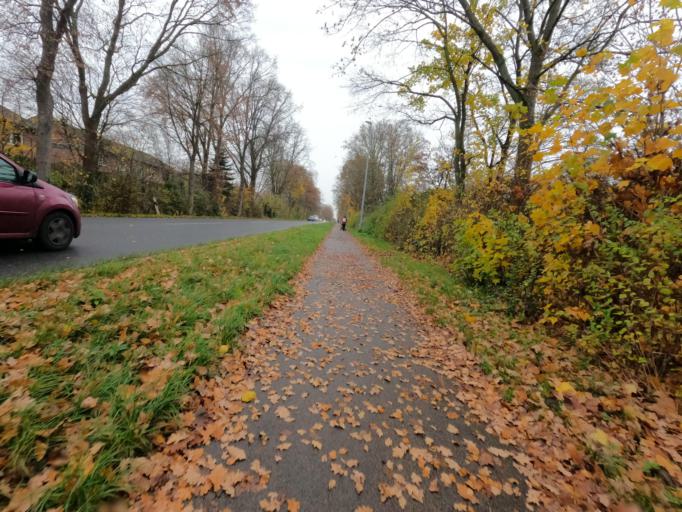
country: DE
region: North Rhine-Westphalia
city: Geilenkirchen
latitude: 50.9738
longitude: 6.1195
